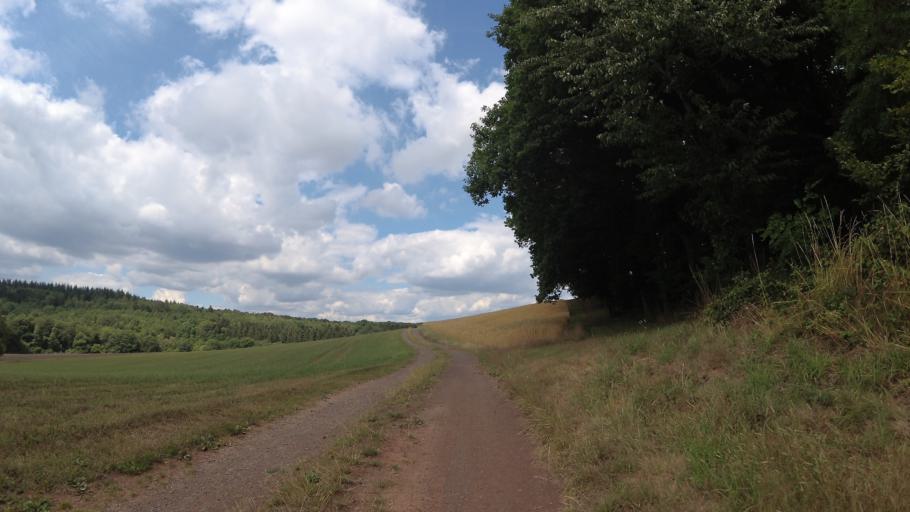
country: DE
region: Saarland
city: Sankt Wendel
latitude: 49.4444
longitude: 7.2119
